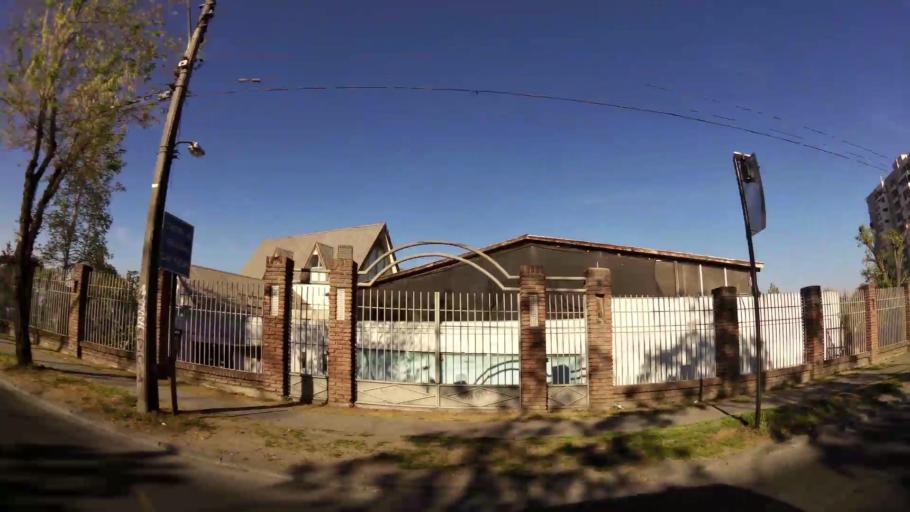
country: CL
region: Santiago Metropolitan
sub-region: Provincia de Santiago
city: Villa Presidente Frei, Nunoa, Santiago, Chile
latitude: -33.4402
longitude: -70.5714
